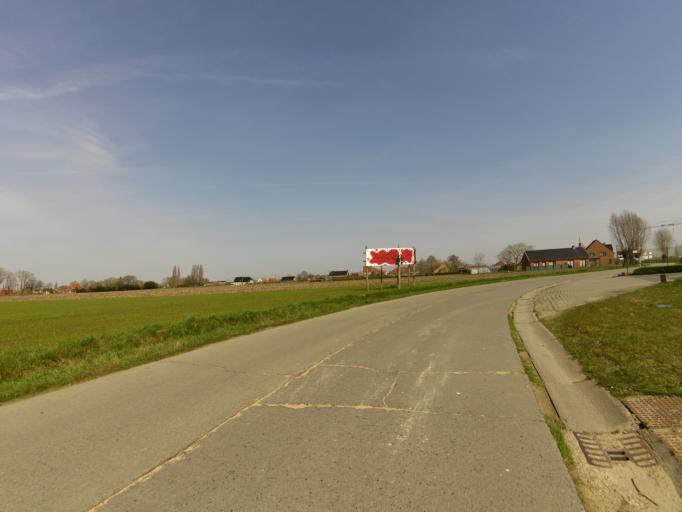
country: BE
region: Flanders
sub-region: Provincie West-Vlaanderen
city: Koekelare
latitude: 51.0954
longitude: 2.9628
